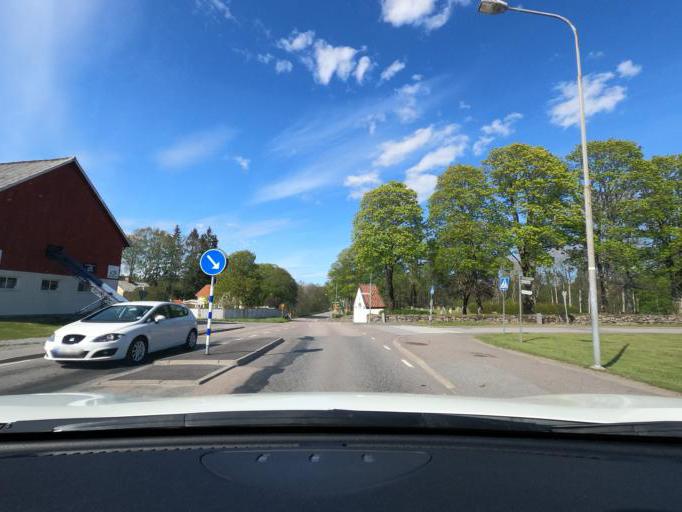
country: SE
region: Vaestra Goetaland
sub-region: Harryda Kommun
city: Ravlanda
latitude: 57.6512
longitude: 12.4924
